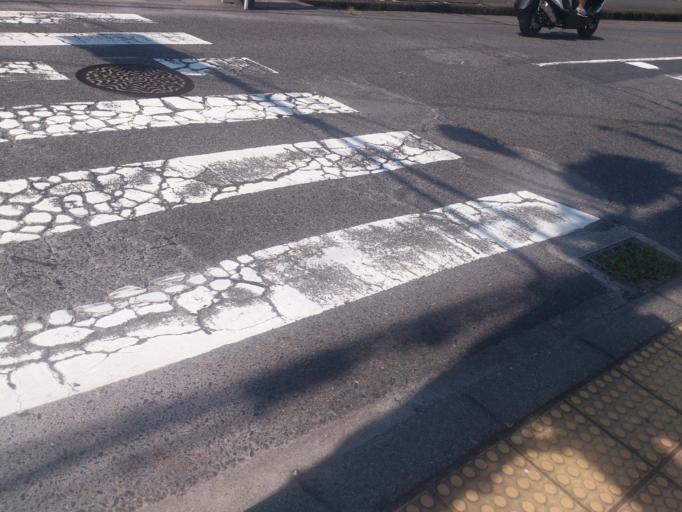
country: JP
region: Shiga Prefecture
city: Otsu-shi
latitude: 35.0027
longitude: 135.8795
